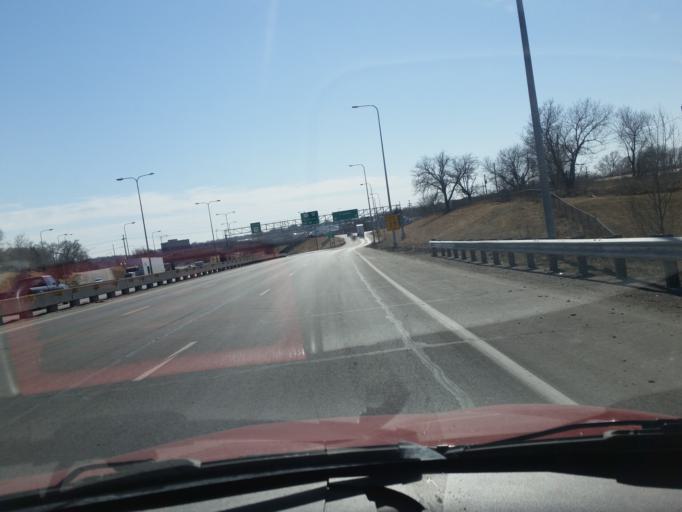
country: US
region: Nebraska
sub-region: Douglas County
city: Omaha
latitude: 41.2222
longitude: -95.9526
